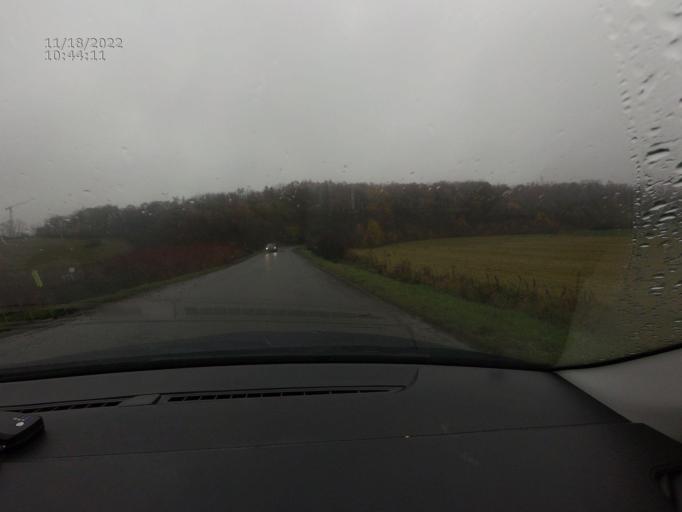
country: CZ
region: Central Bohemia
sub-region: Okres Beroun
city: Horovice
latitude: 49.8427
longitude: 13.9107
